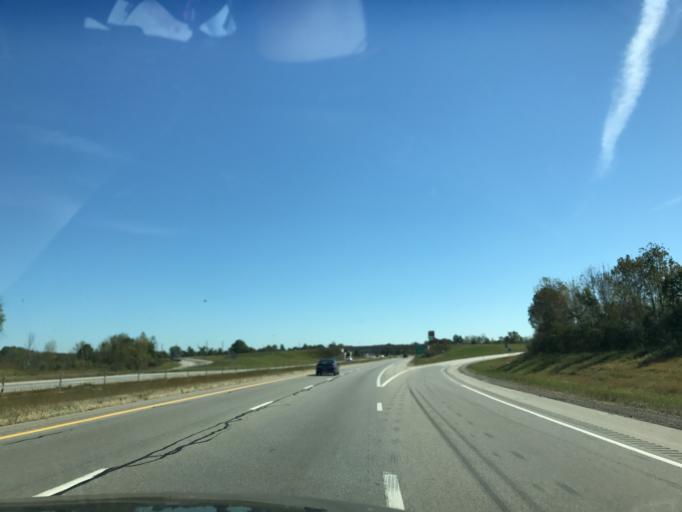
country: US
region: Ohio
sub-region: Licking County
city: Etna
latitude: 39.9456
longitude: -82.6047
